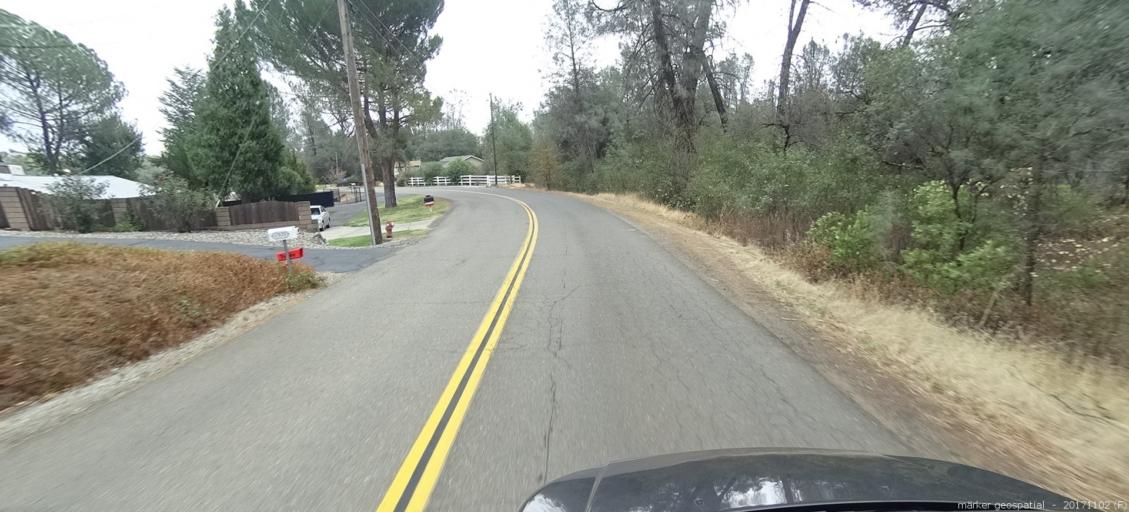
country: US
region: California
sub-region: Shasta County
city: Central Valley (historical)
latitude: 40.6622
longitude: -122.3994
